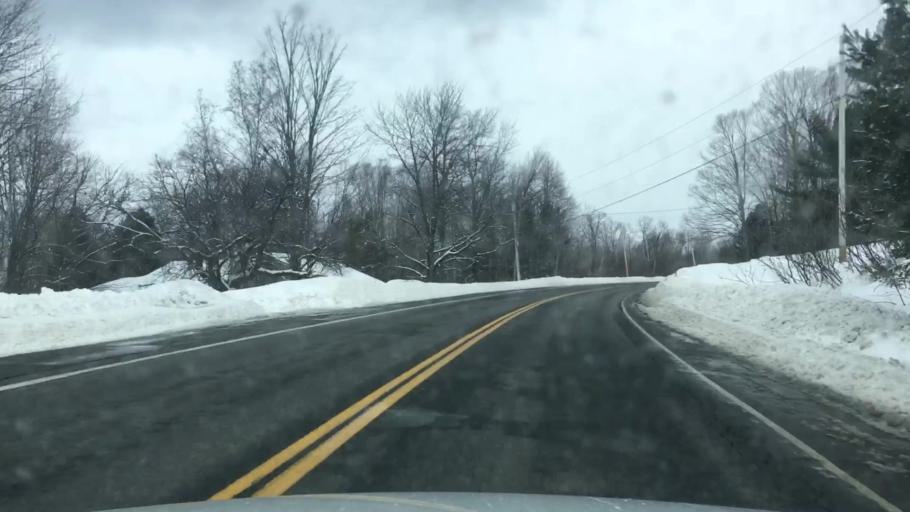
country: US
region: Maine
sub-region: Somerset County
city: Cornville
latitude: 44.8173
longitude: -69.7067
